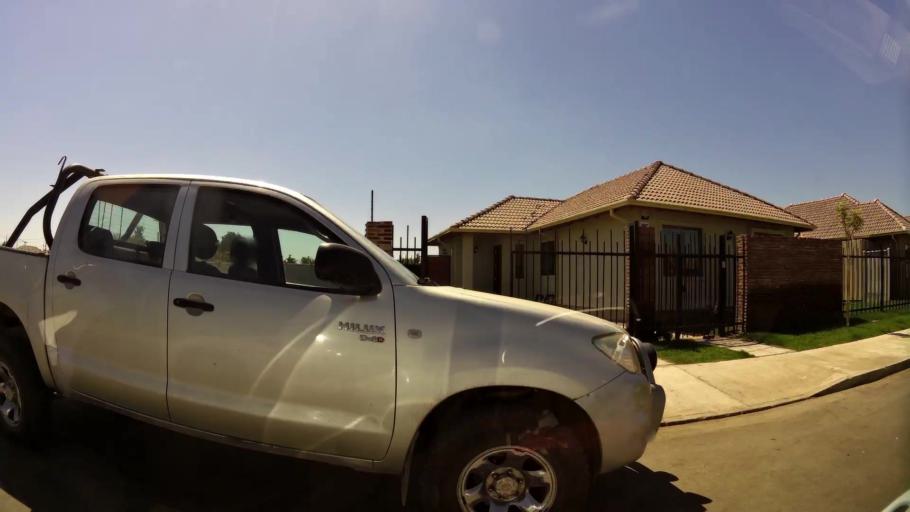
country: CL
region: Maule
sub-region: Provincia de Talca
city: Talca
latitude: -35.4323
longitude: -71.5941
